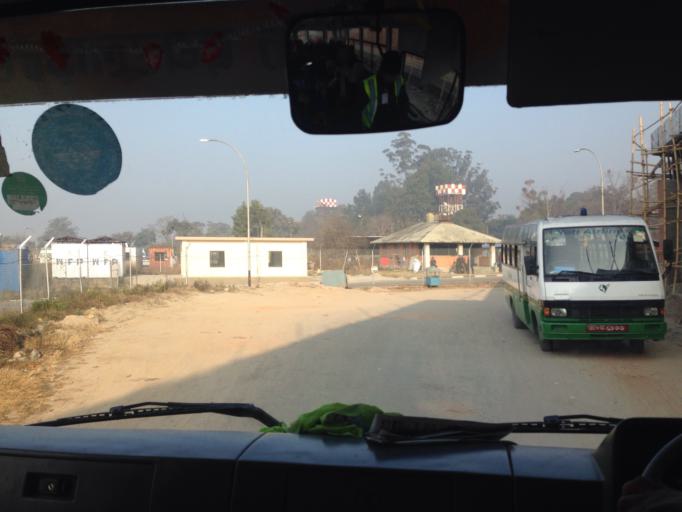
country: NP
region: Central Region
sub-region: Bagmati Zone
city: Kathmandu
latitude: 27.7024
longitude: 85.3589
